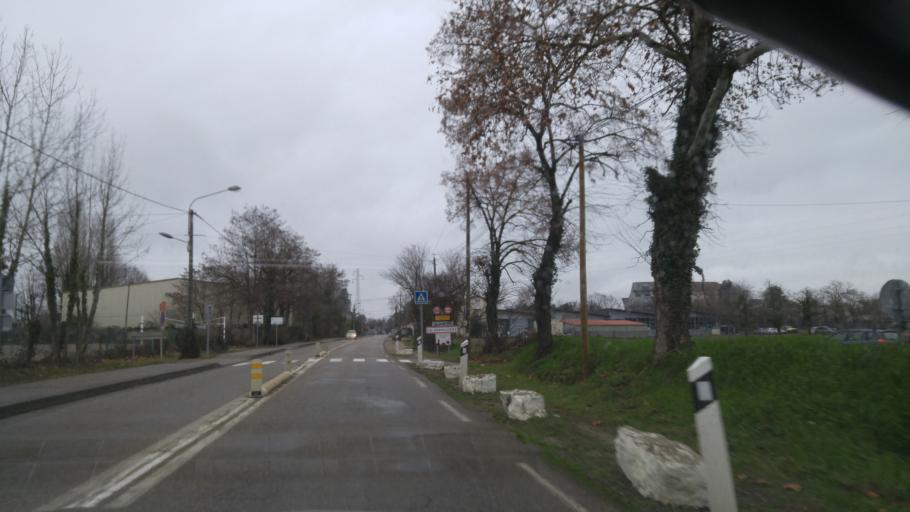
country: FR
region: Rhone-Alpes
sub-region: Departement de l'Isere
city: Villefontaine
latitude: 45.6245
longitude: 5.1539
